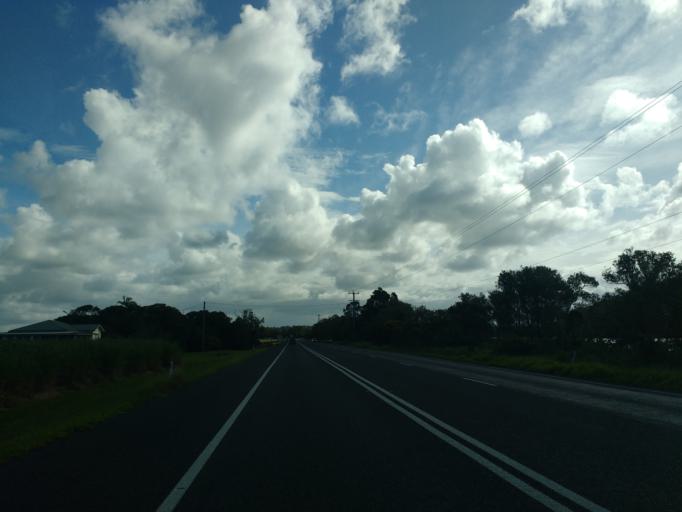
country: AU
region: New South Wales
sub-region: Richmond Valley
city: Evans Head
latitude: -28.9984
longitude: 153.4471
